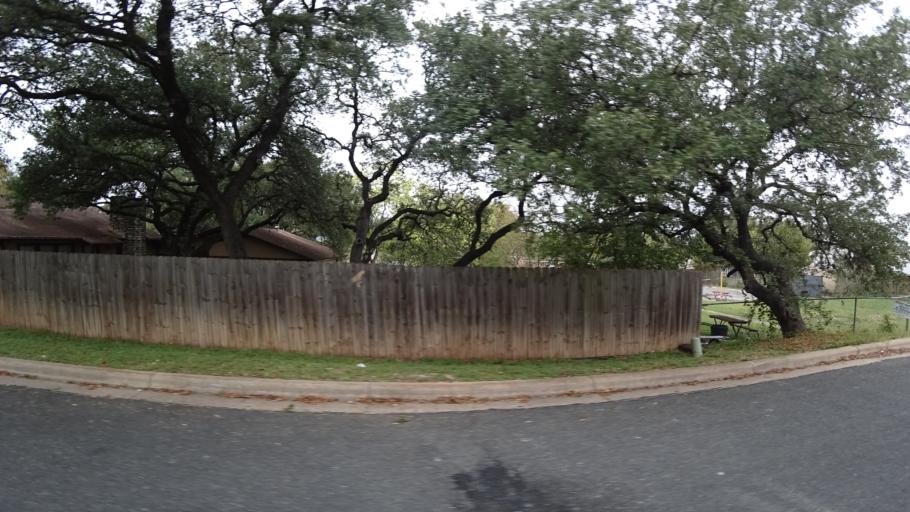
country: US
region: Texas
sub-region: Travis County
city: Barton Creek
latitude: 30.2345
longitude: -97.8797
